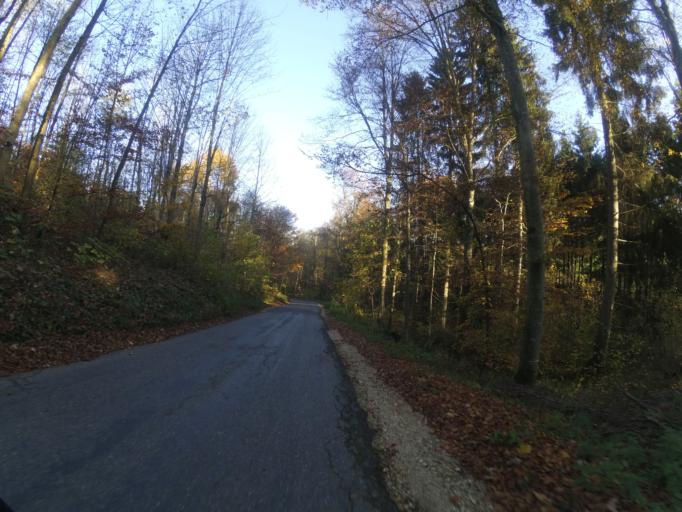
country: DE
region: Baden-Wuerttemberg
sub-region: Tuebingen Region
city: Berghulen
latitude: 48.4784
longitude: 9.8056
